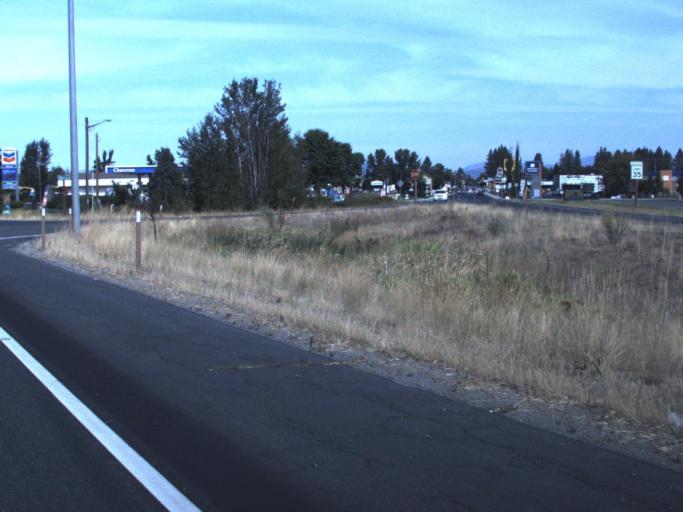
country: US
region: Washington
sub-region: Spokane County
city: Deer Park
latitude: 47.9424
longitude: -117.4771
